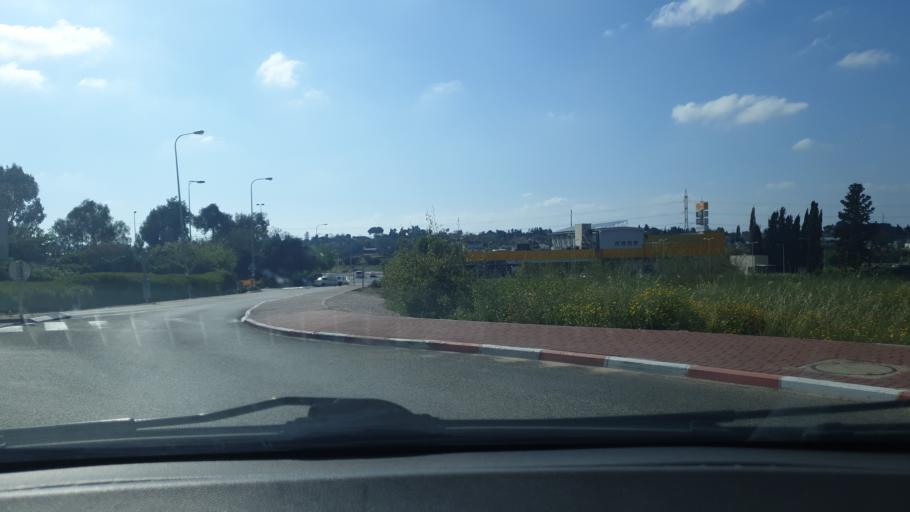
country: IL
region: Central District
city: Bet Yizhaq
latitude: 32.3446
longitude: 34.9103
